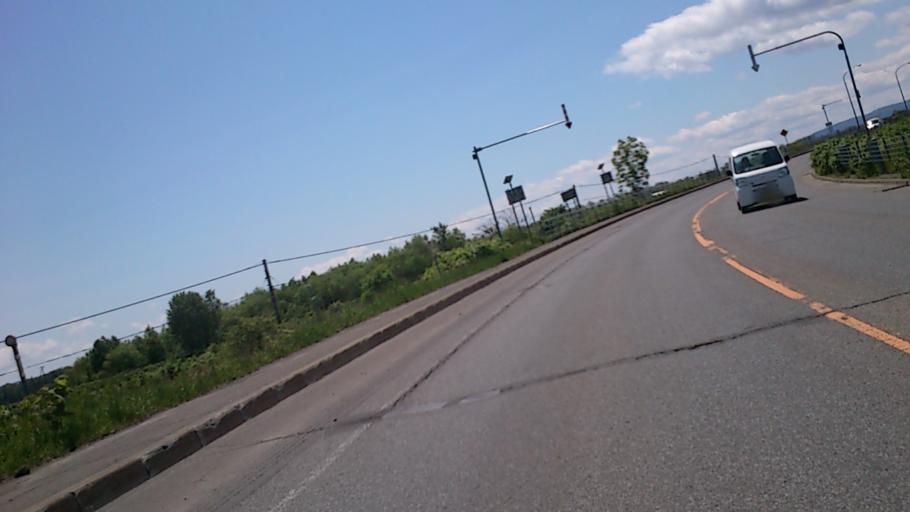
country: JP
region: Hokkaido
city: Nayoro
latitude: 44.3148
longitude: 142.4568
